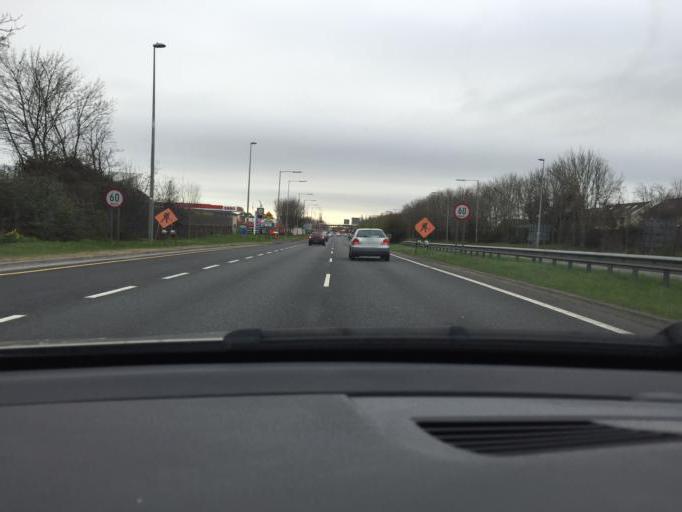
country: IE
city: Palmerstown
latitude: 53.3564
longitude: -6.3772
